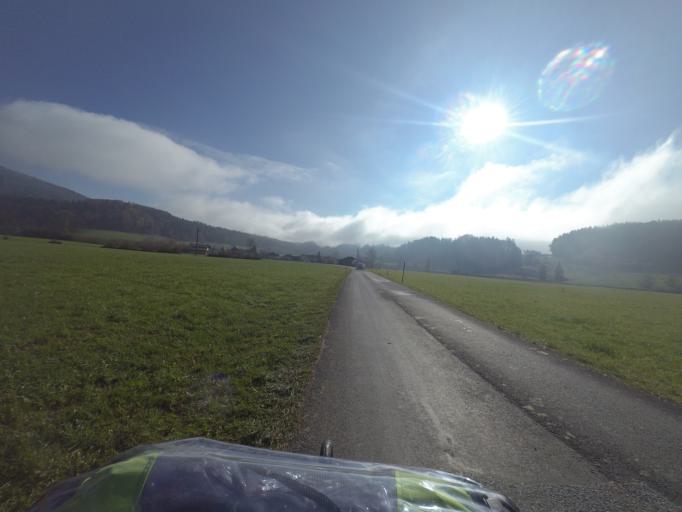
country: AT
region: Salzburg
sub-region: Politischer Bezirk Hallein
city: Adnet
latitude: 47.6862
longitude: 13.1403
